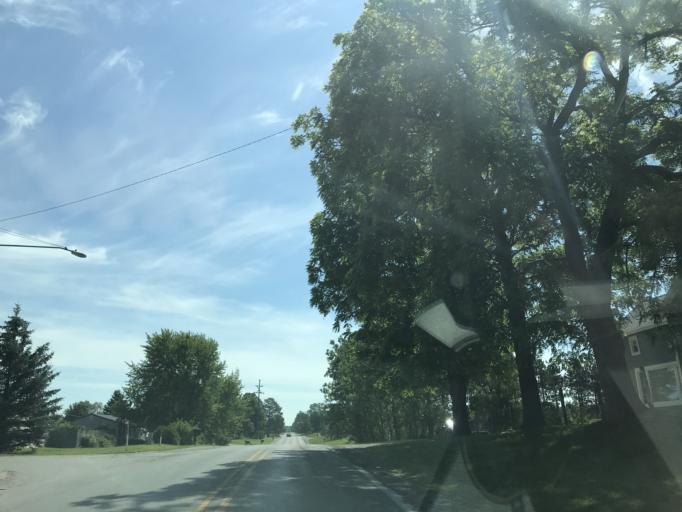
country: US
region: Michigan
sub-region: Grand Traverse County
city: Traverse City
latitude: 44.6575
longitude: -85.6614
